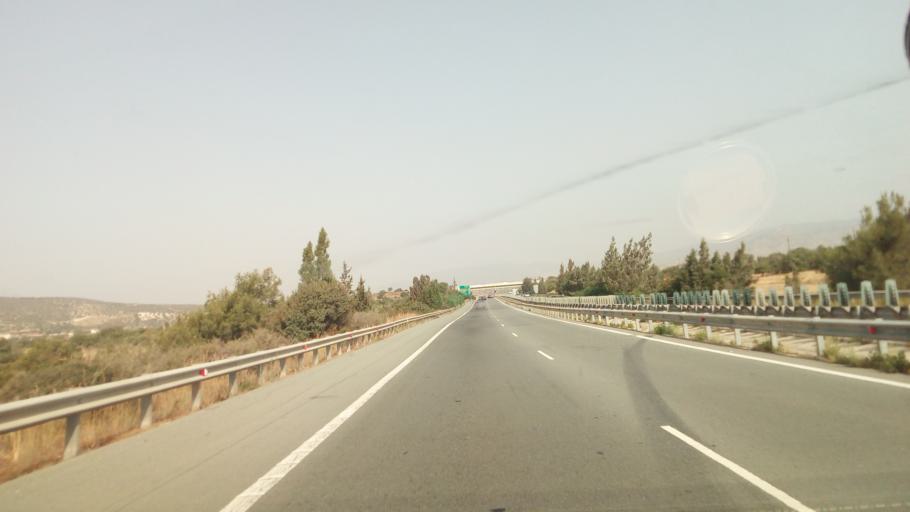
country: CY
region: Limassol
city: Pyrgos
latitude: 34.7263
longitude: 33.2428
